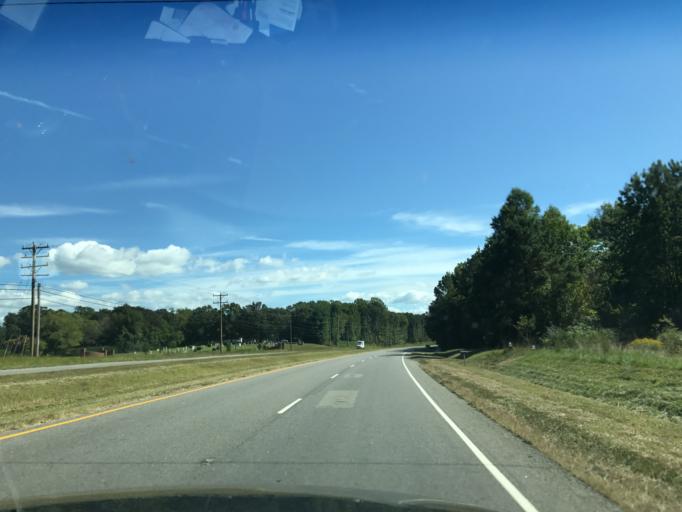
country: US
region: Virginia
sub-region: Essex County
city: Tappahannock
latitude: 37.8503
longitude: -76.8068
